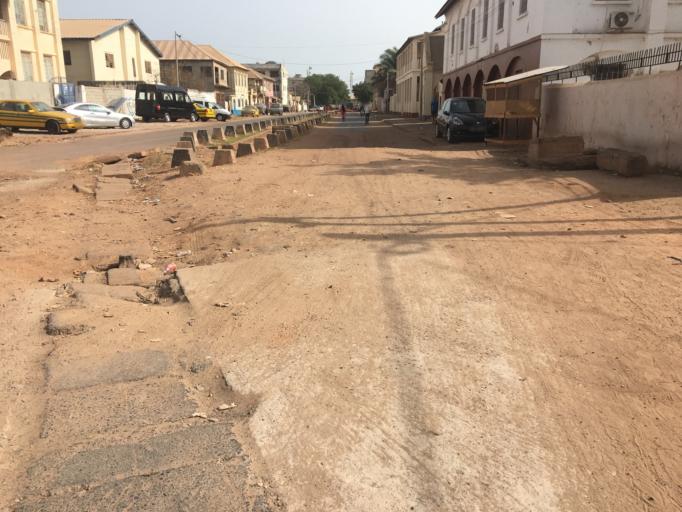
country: GM
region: Banjul
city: Banjul
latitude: 13.4523
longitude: -16.5756
